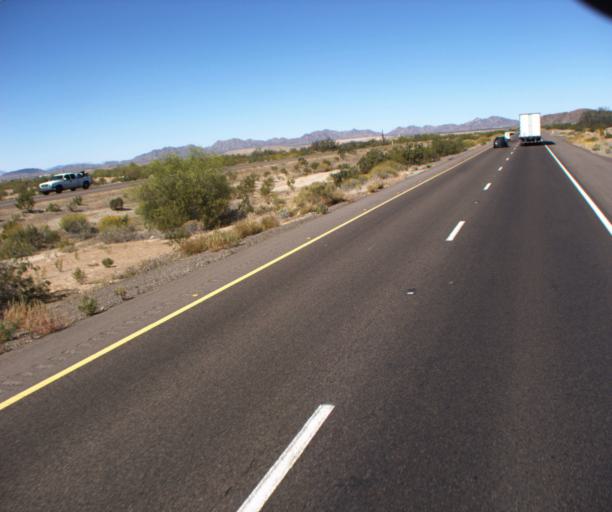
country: US
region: Arizona
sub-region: Maricopa County
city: Gila Bend
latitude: 33.1381
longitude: -112.6500
